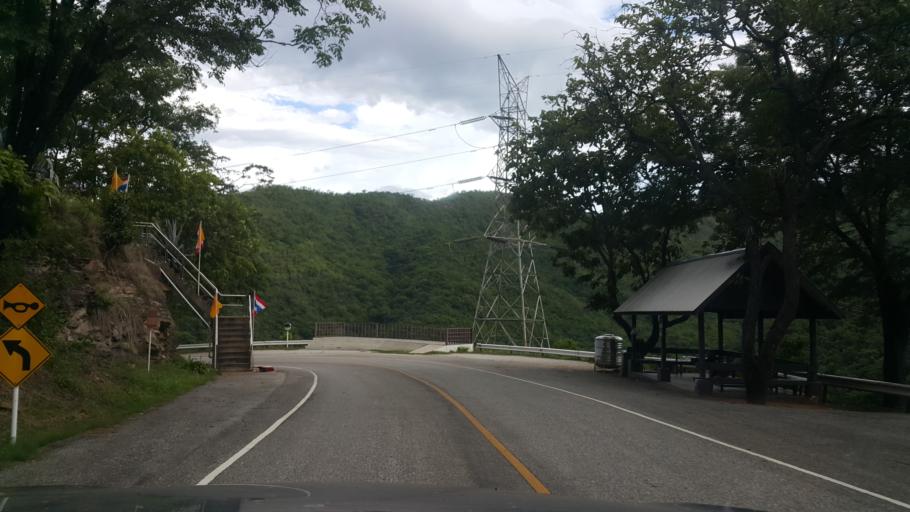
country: TH
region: Tak
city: Sam Ngao
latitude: 17.2426
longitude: 98.9835
